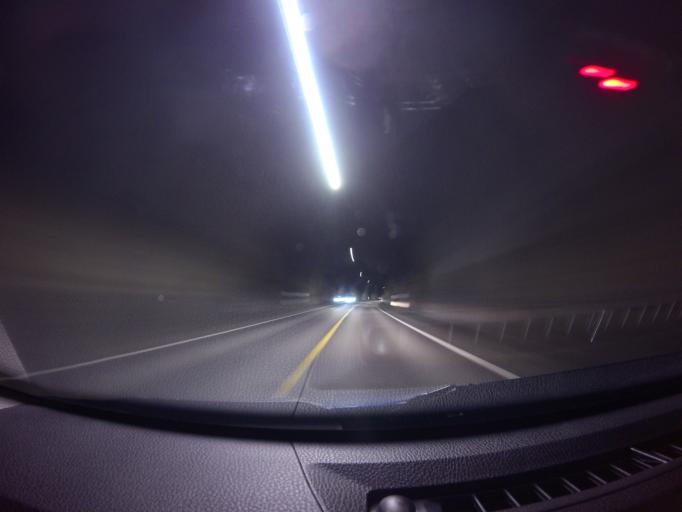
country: NO
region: Rogaland
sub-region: Forsand
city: Forsand
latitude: 58.8354
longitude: 6.2800
